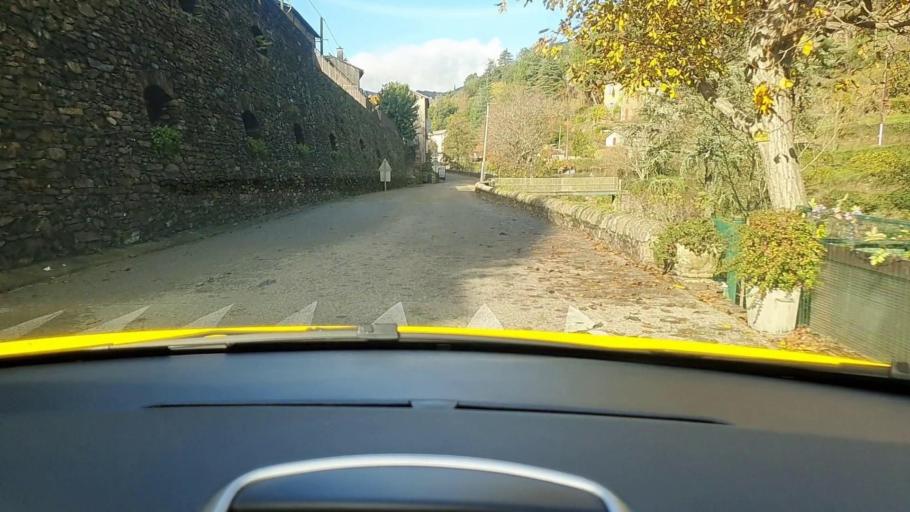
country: FR
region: Languedoc-Roussillon
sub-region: Departement du Gard
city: Valleraugue
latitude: 44.1541
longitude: 3.6881
